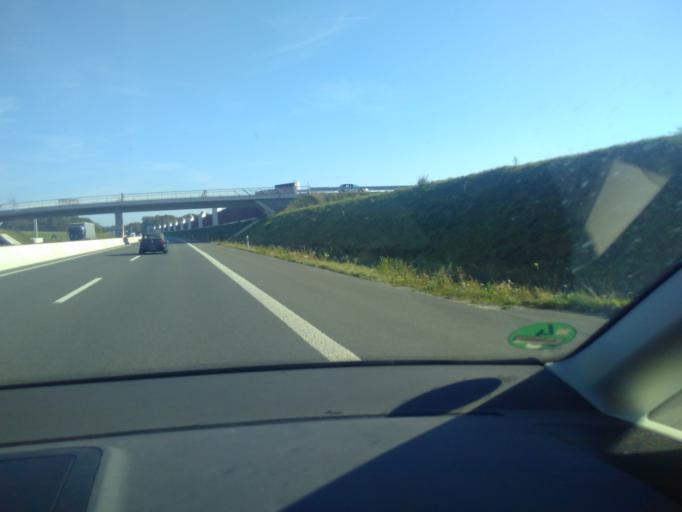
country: DE
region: North Rhine-Westphalia
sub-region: Regierungsbezirk Detmold
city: Steinhagen
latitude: 52.0155
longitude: 8.4005
